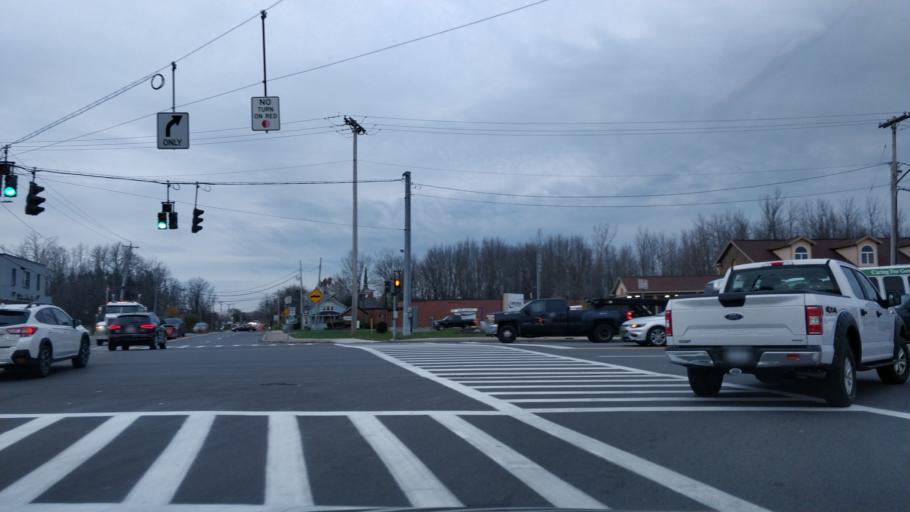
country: US
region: New York
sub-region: Onondaga County
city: North Syracuse
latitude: 43.1752
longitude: -76.1191
